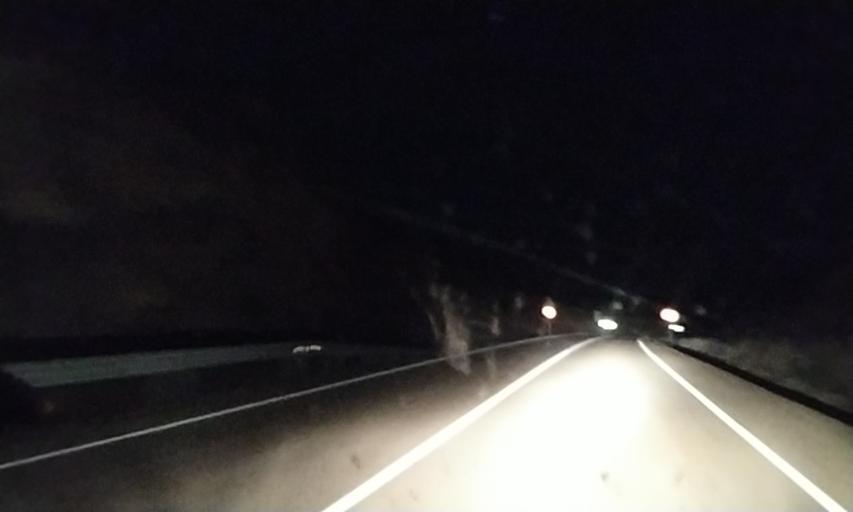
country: ES
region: Castille and Leon
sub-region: Provincia de Salamanca
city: Herguijuela de Ciudad Rodrigo
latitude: 40.4839
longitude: -6.5810
